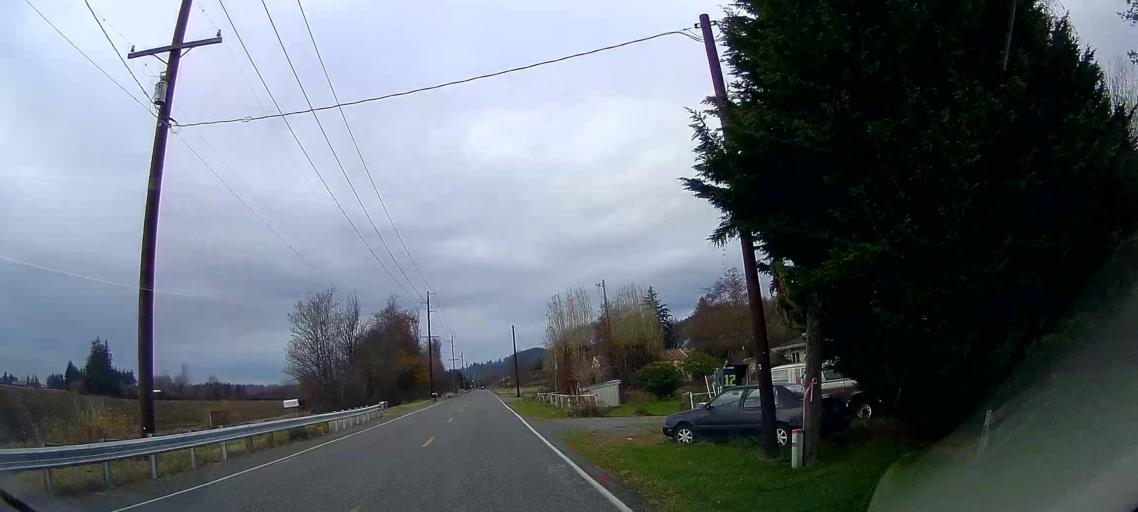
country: US
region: Washington
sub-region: Skagit County
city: Sedro-Woolley
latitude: 48.5184
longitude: -122.2619
